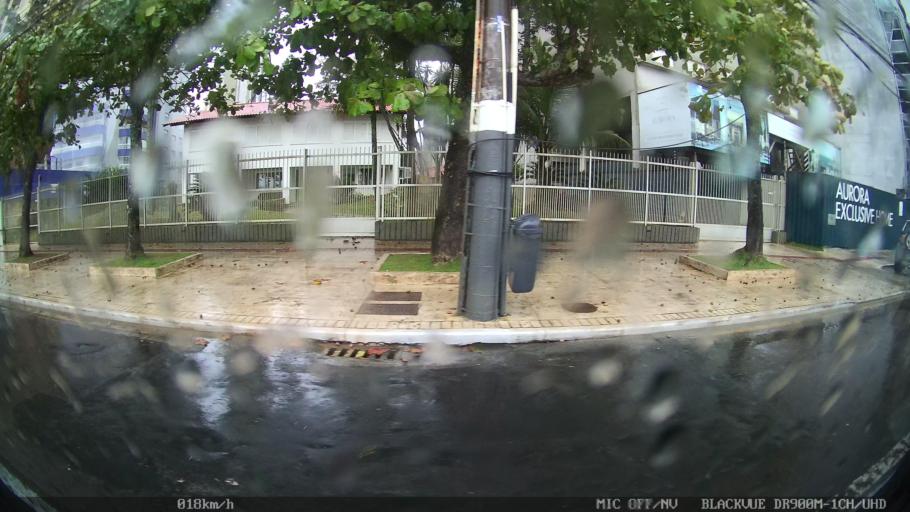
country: BR
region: Santa Catarina
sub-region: Balneario Camboriu
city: Balneario Camboriu
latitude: -27.0043
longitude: -48.6166
